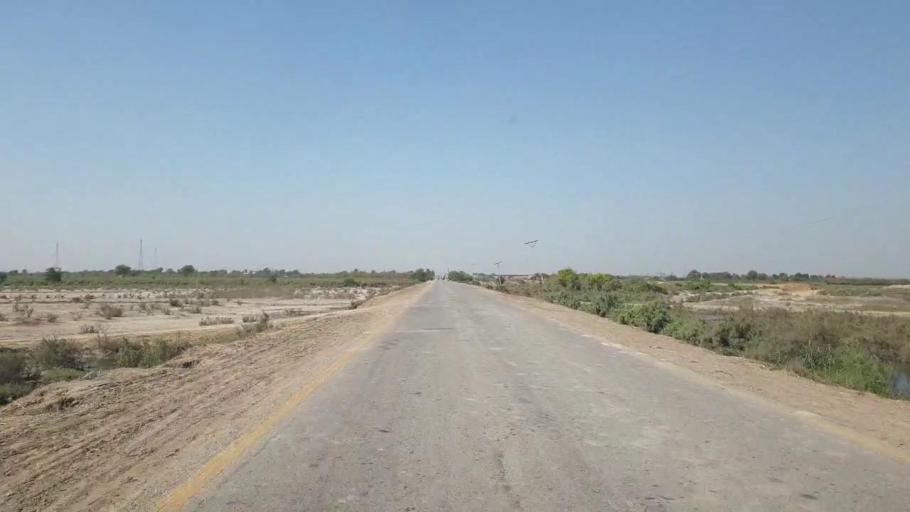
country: PK
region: Sindh
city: Rajo Khanani
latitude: 25.0551
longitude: 68.8045
